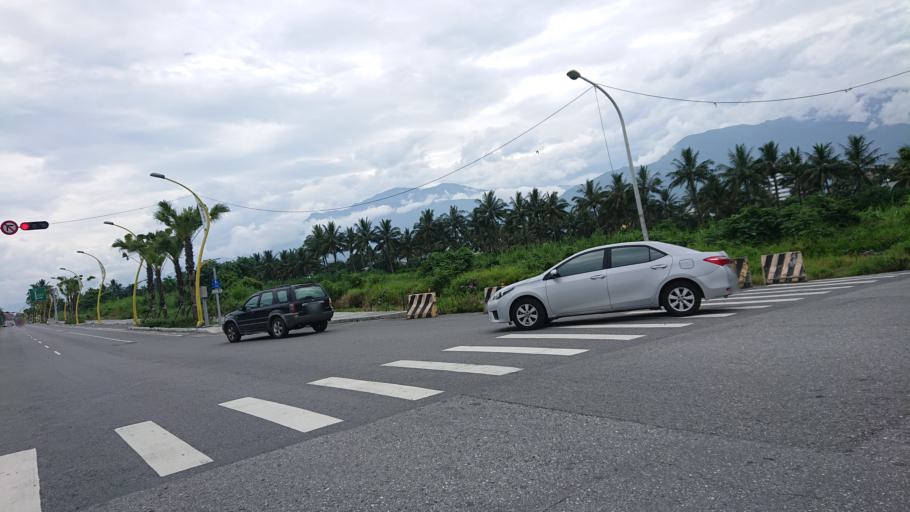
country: TW
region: Taiwan
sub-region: Hualien
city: Hualian
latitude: 23.9695
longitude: 121.6109
